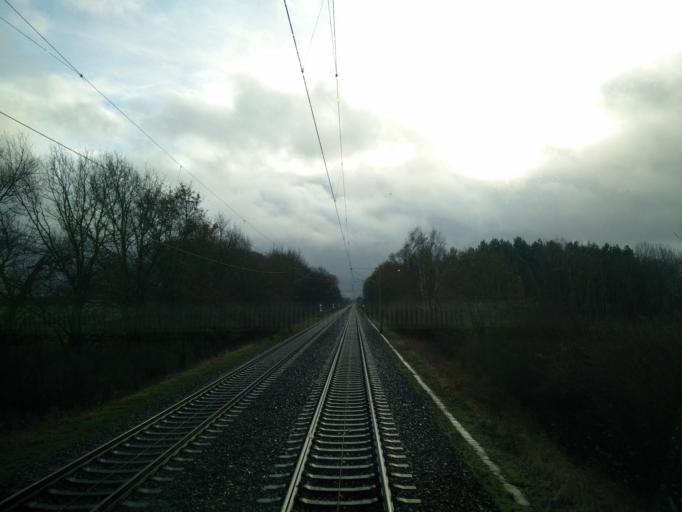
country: DE
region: Brandenburg
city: Karstadt
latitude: 53.1845
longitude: 11.7349
